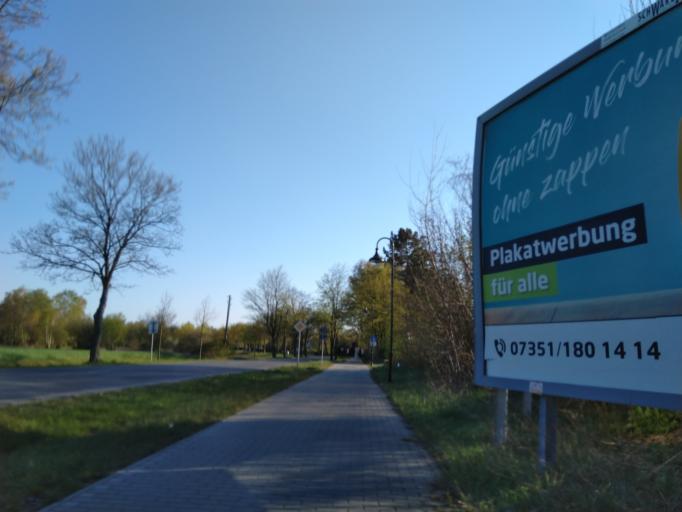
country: DE
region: Brandenburg
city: Bernau bei Berlin
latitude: 52.6645
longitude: 13.5577
